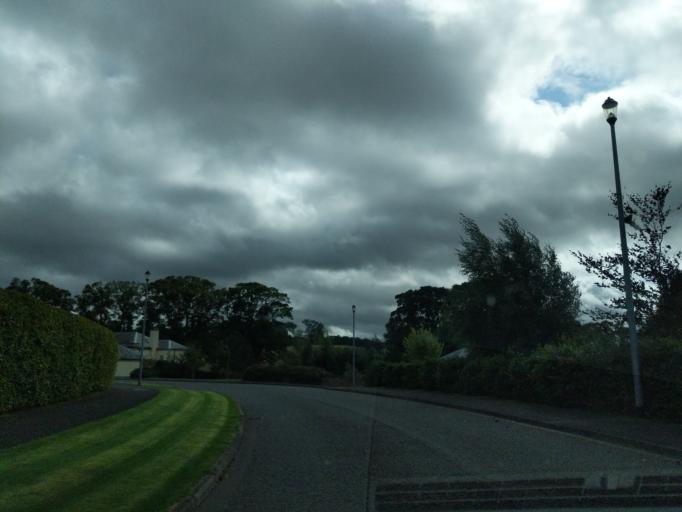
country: GB
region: Scotland
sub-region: The Scottish Borders
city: Kelso
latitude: 55.5639
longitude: -2.4708
